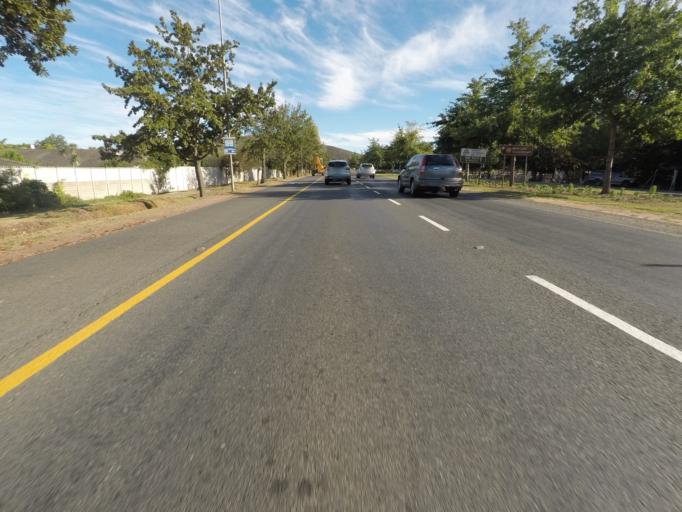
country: ZA
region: Western Cape
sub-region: Cape Winelands District Municipality
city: Stellenbosch
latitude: -33.9473
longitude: 18.8536
